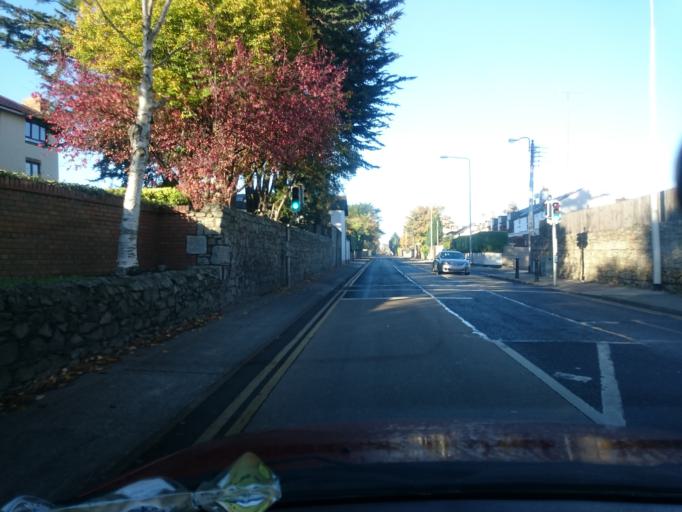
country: IE
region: Leinster
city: Monkstown
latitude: 53.2947
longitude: -6.1610
